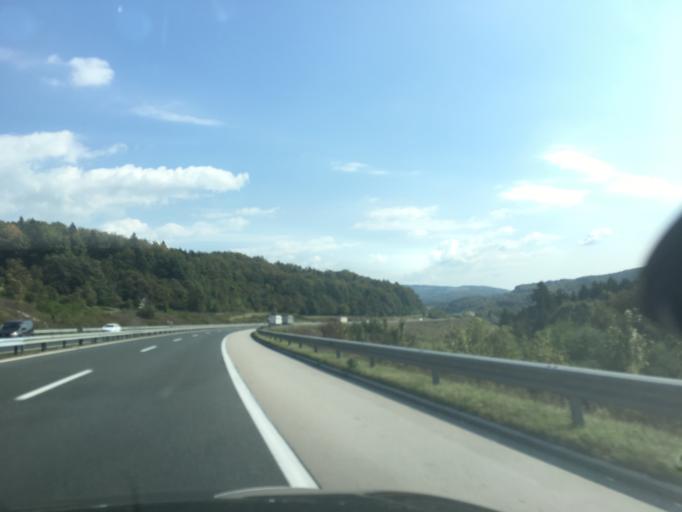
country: SI
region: Ivancna Gorica
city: Sentvid pri Sticni
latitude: 45.9305
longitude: 14.9233
